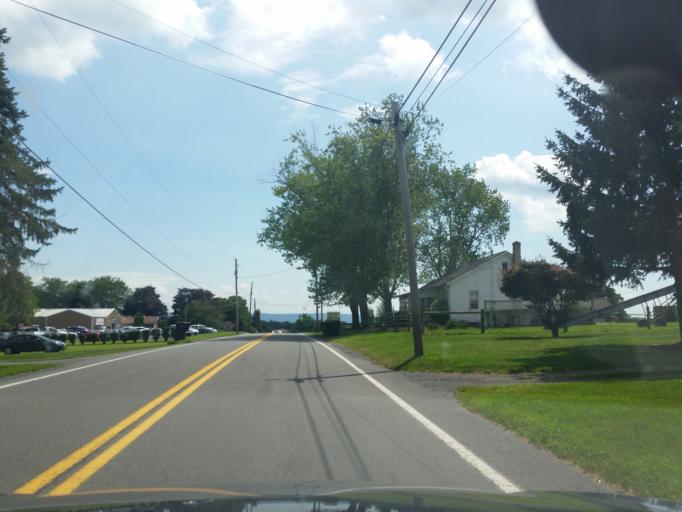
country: US
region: Pennsylvania
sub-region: Dauphin County
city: Elizabethville
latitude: 40.5061
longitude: -76.8803
